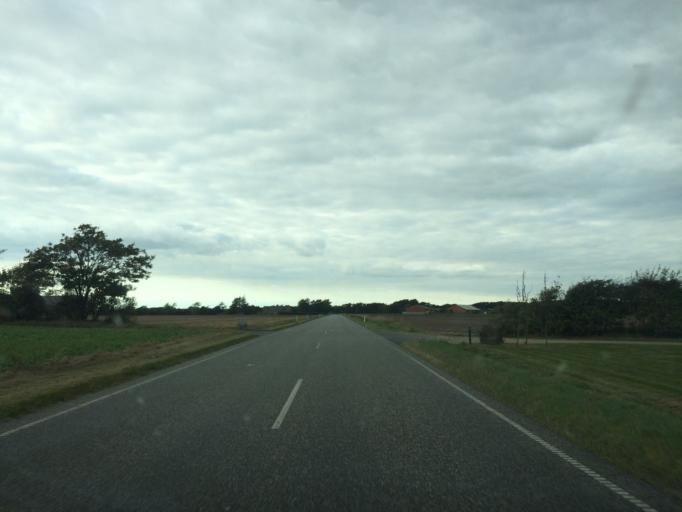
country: DK
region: Central Jutland
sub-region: Ringkobing-Skjern Kommune
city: Ringkobing
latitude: 56.1051
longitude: 8.3247
